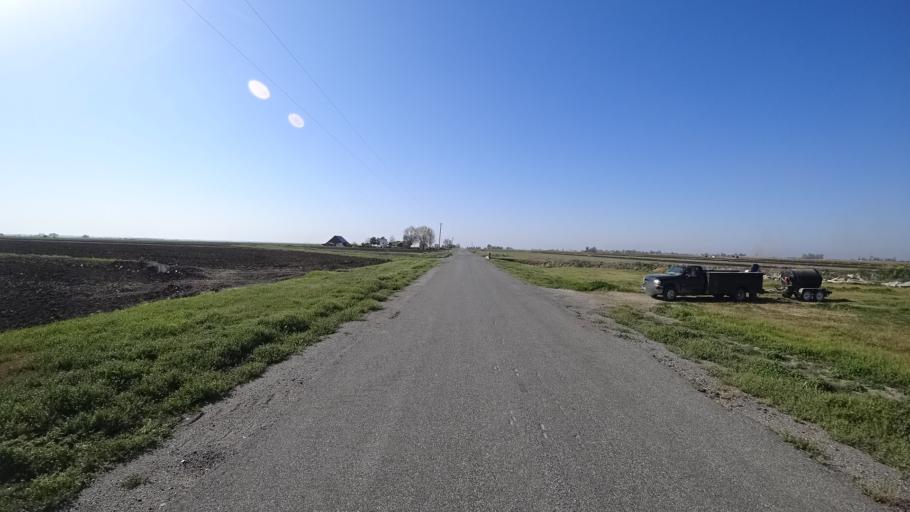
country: US
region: California
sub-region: Glenn County
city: Willows
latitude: 39.5723
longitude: -122.0839
